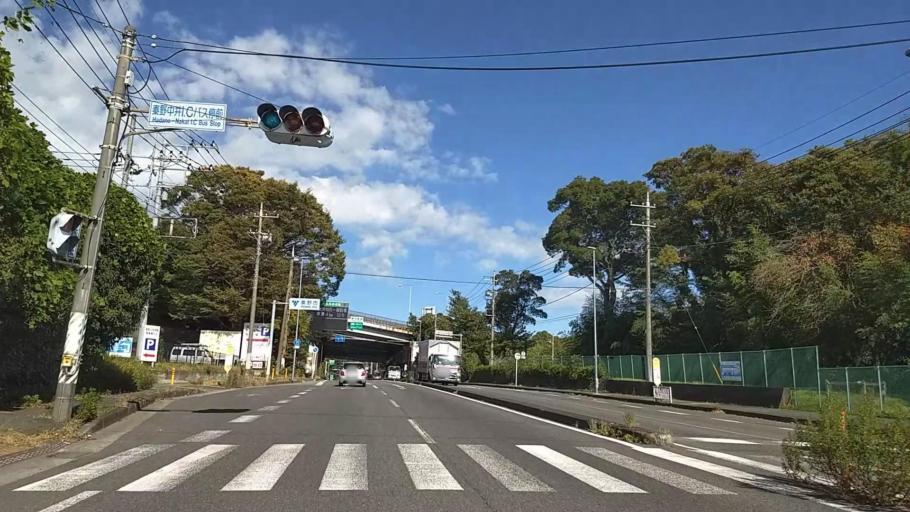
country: JP
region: Kanagawa
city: Hadano
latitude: 35.3517
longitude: 139.2358
